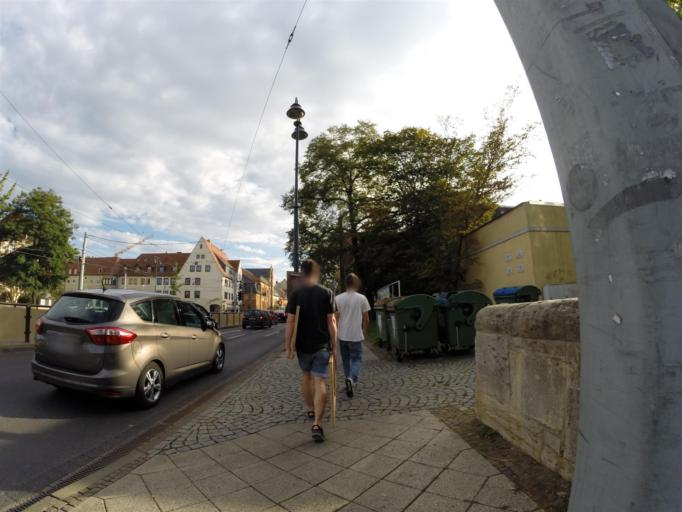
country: DE
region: Thuringia
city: Jena
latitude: 50.9292
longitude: 11.5905
